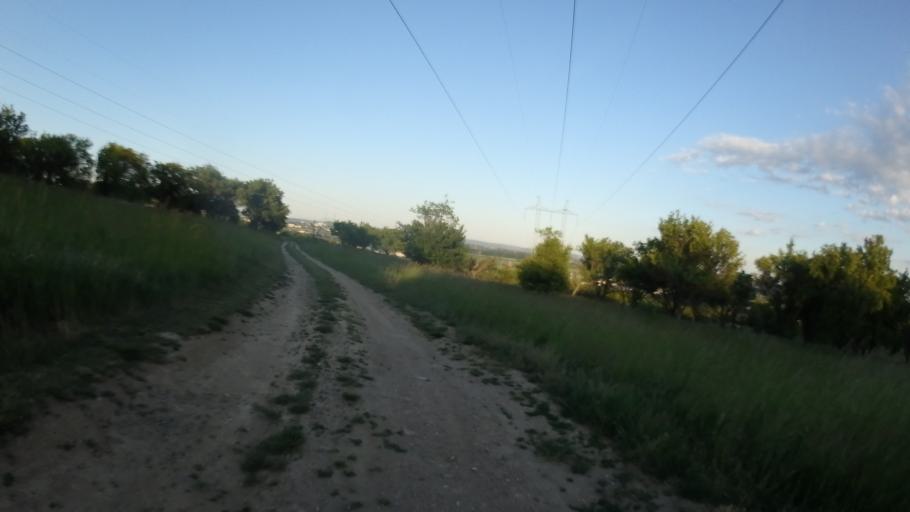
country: CZ
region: South Moravian
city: Zelesice
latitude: 49.1248
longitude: 16.5902
